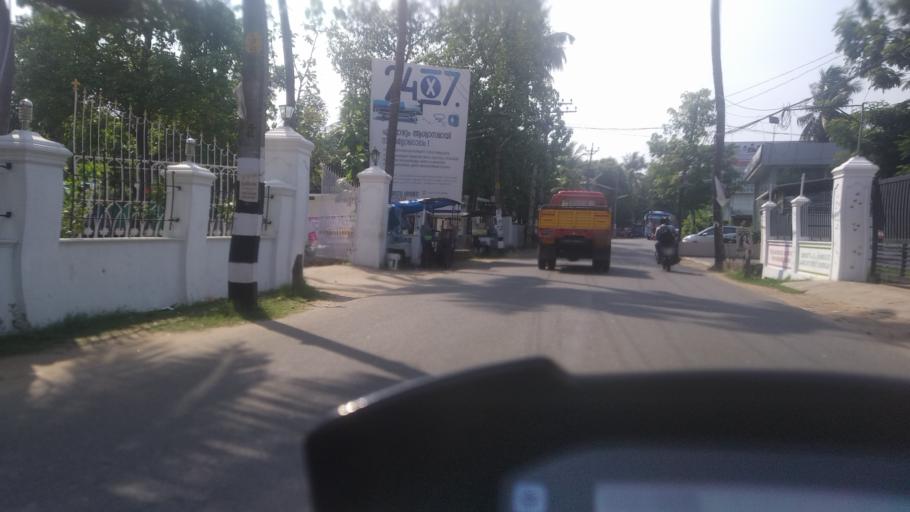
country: IN
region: Kerala
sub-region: Ernakulam
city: Elur
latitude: 10.0521
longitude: 76.2157
